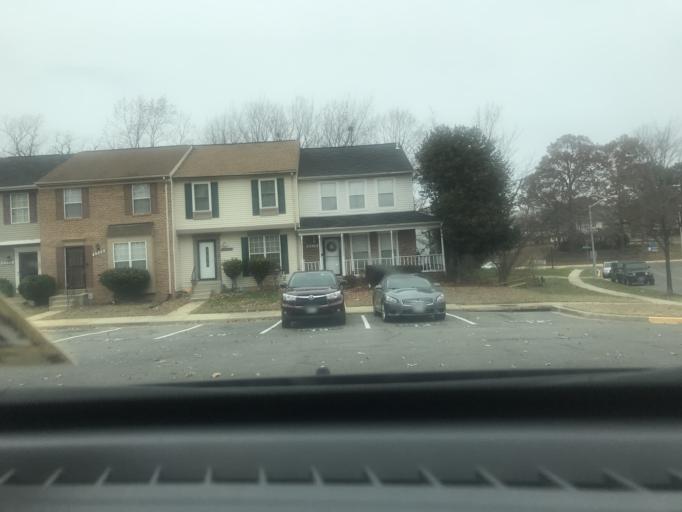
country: US
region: Maryland
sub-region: Prince George's County
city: Hillcrest Heights
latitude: 38.8136
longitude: -76.9667
